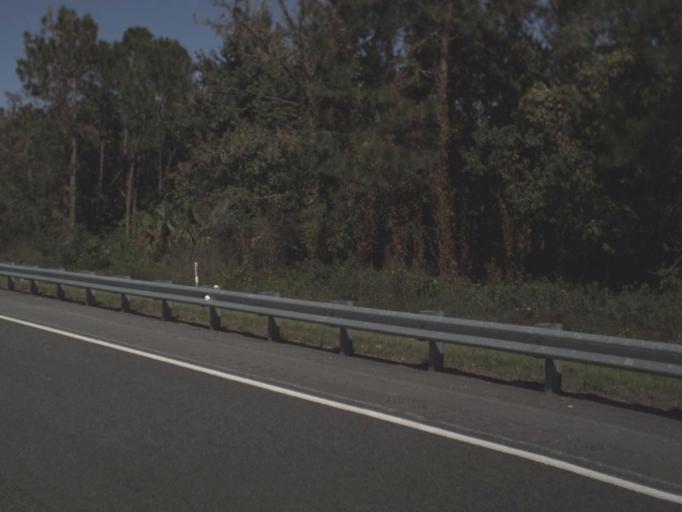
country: US
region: Florida
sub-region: Seminole County
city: Sanford
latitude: 28.7644
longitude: -81.2716
